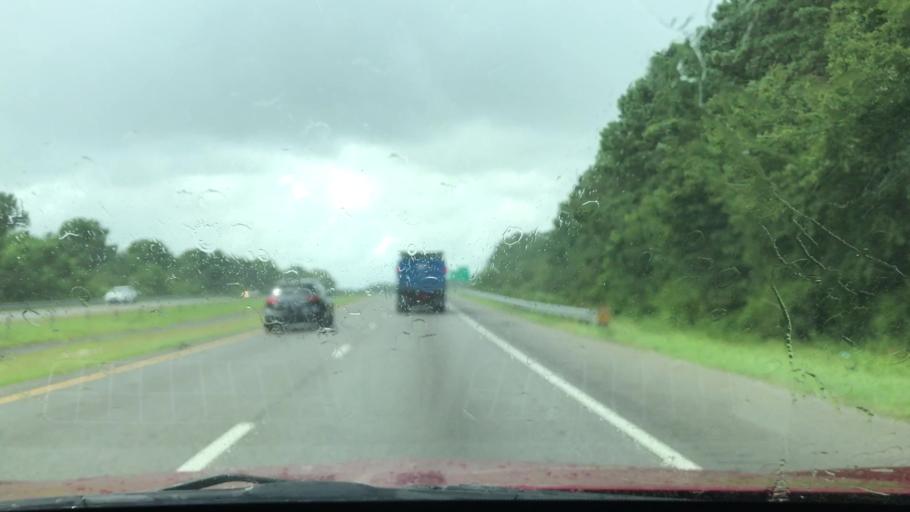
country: US
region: South Carolina
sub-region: Charleston County
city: Mount Pleasant
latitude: 32.8286
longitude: -79.8514
